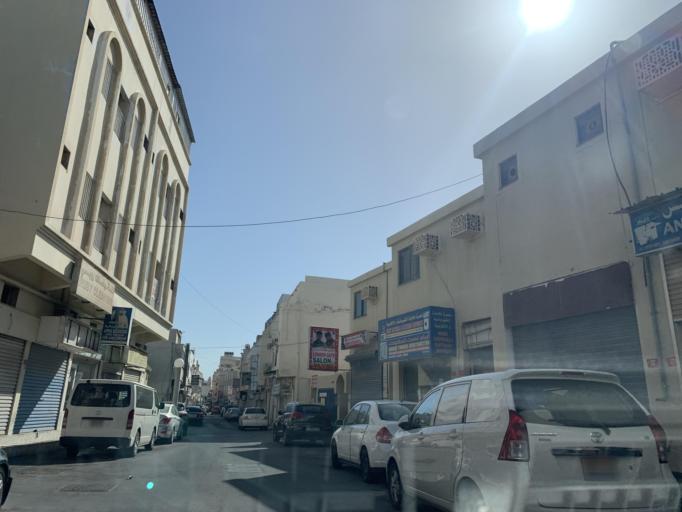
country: BH
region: Muharraq
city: Al Muharraq
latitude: 26.2487
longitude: 50.6126
